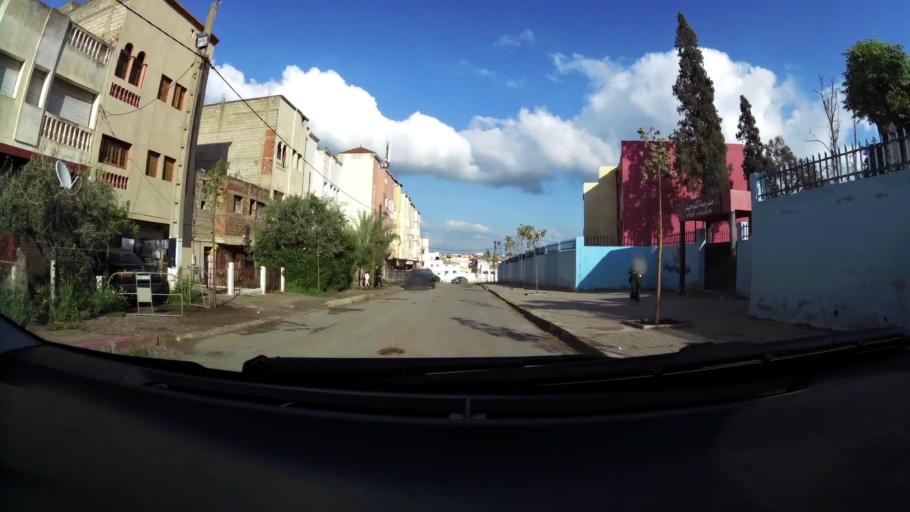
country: MA
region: Chaouia-Ouardigha
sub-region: Settat Province
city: Settat
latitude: 33.0071
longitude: -7.6256
